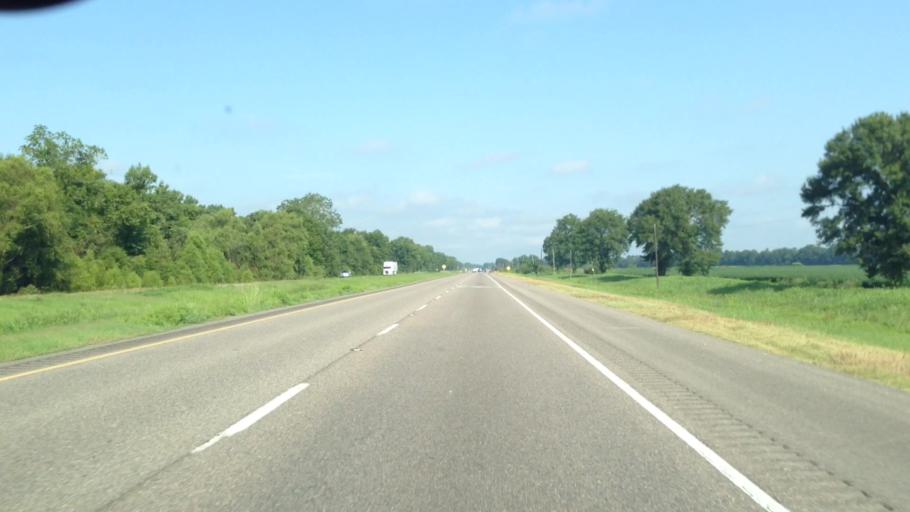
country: US
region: Louisiana
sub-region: West Baton Rouge Parish
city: Erwinville
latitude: 30.5200
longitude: -91.3678
